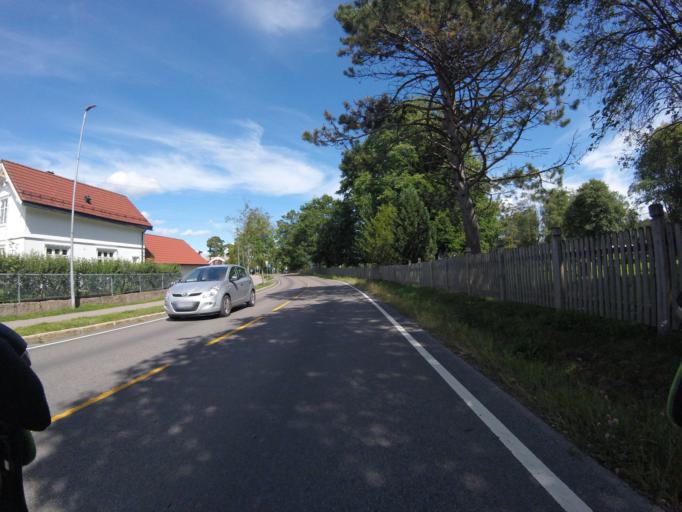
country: NO
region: Akershus
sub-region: Skedsmo
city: Lillestrom
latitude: 59.9447
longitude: 11.0188
